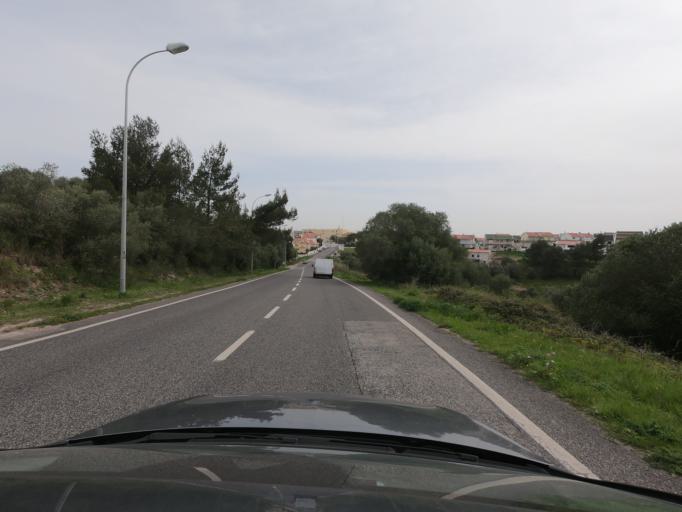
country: PT
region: Lisbon
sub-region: Oeiras
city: Barcarena
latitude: 38.7265
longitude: -9.2877
